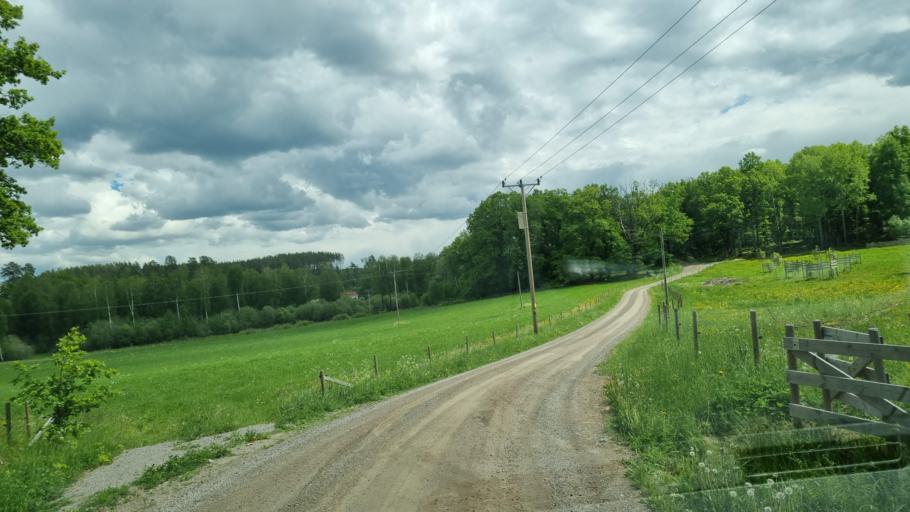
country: SE
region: OEstergoetland
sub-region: Atvidabergs Kommun
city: Atvidaberg
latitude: 58.1926
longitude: 16.0340
